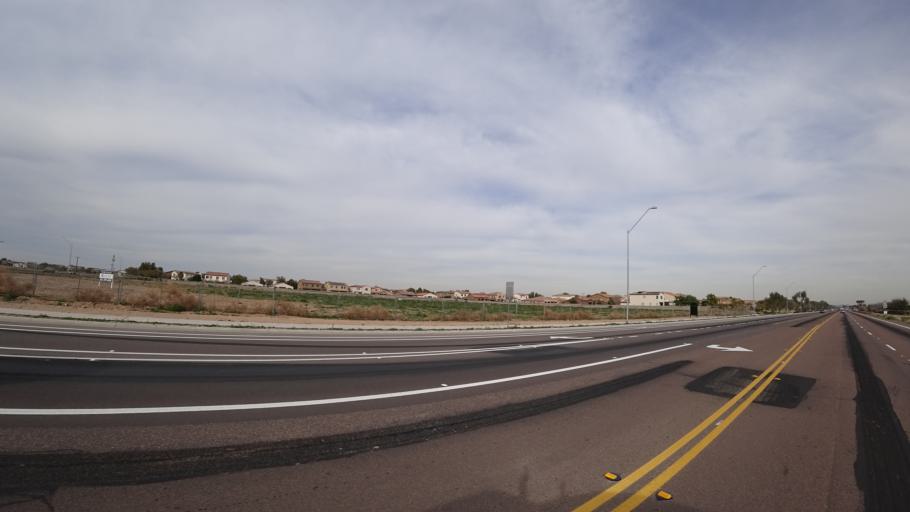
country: US
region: Arizona
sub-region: Maricopa County
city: Citrus Park
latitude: 33.5807
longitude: -112.4091
